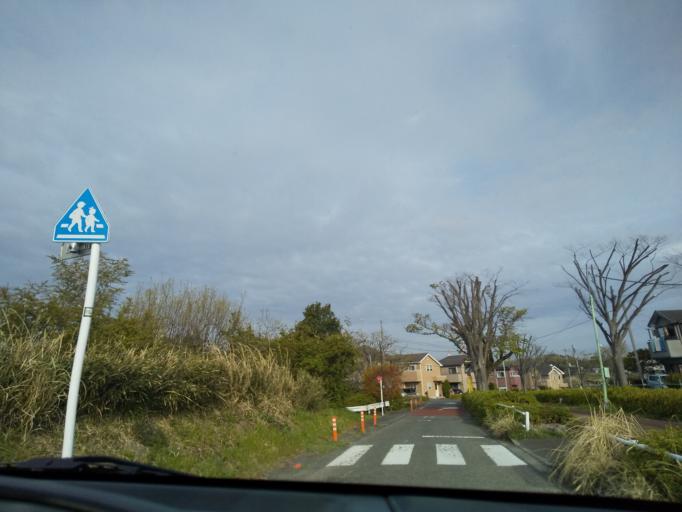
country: JP
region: Tokyo
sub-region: Machida-shi
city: Machida
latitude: 35.5913
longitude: 139.3956
